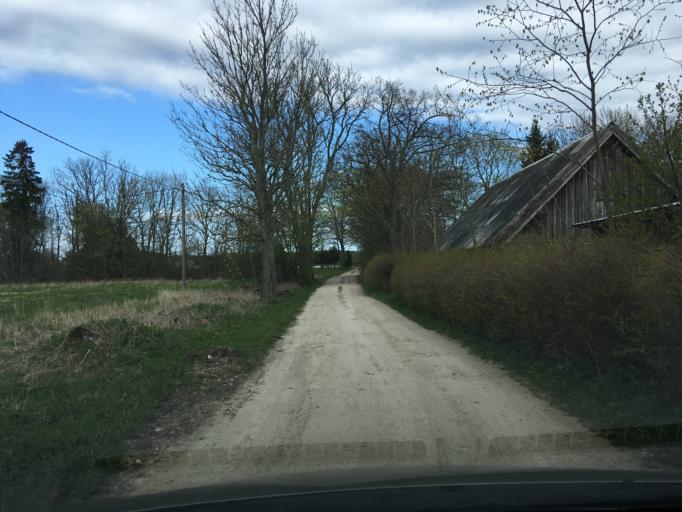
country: EE
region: Laeaene
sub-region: Lihula vald
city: Lihula
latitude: 58.5746
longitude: 23.7238
